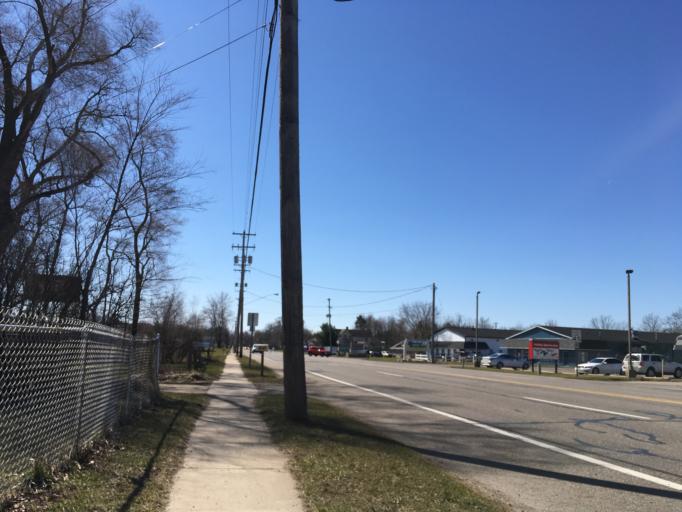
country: US
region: Michigan
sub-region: Kalamazoo County
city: Portage
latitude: 42.1753
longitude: -85.5676
